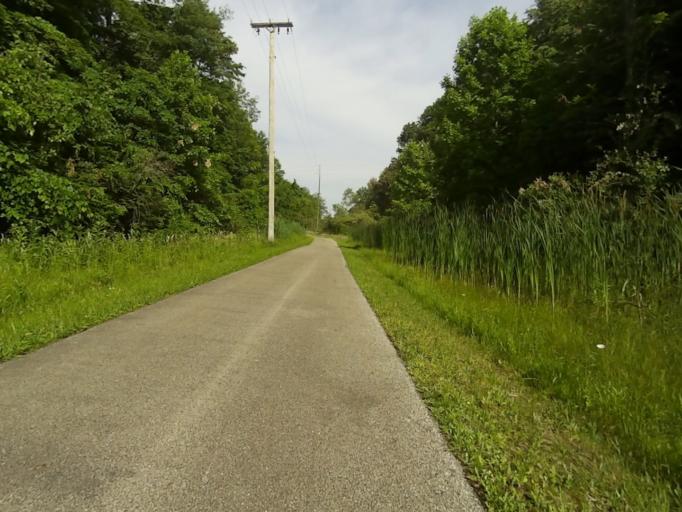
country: US
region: Ohio
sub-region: Summit County
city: Boston Heights
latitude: 41.2272
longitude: -81.4863
